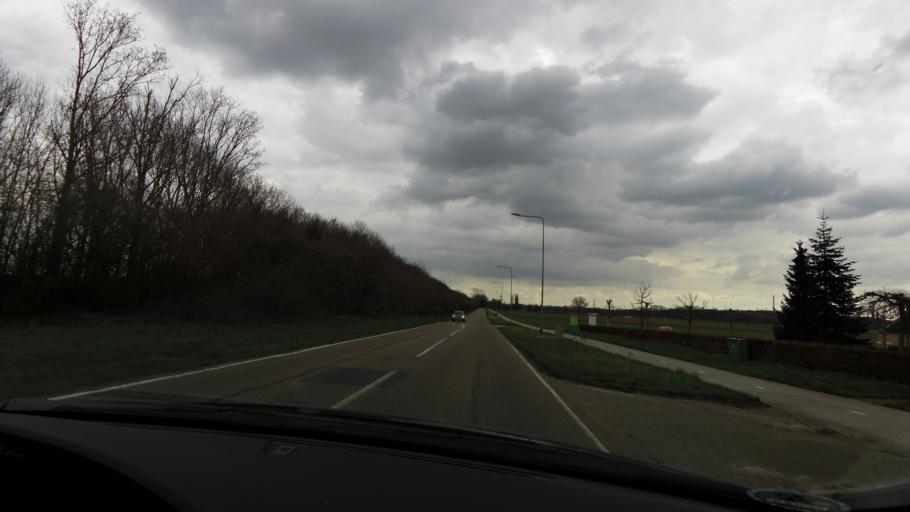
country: NL
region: Limburg
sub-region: Gemeente Stein
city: Berg
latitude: 51.0030
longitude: 5.7794
